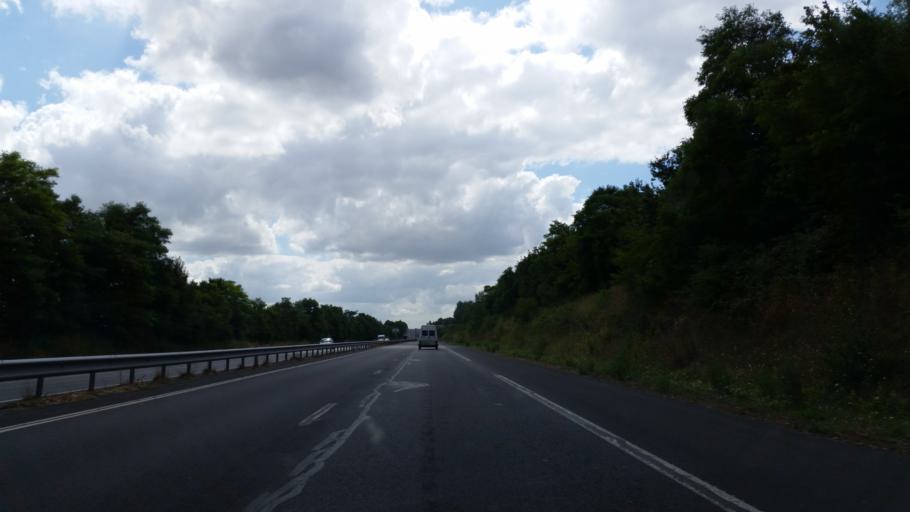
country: FR
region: Lower Normandy
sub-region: Departement du Calvados
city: Falaise
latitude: 48.9051
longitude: -0.2136
